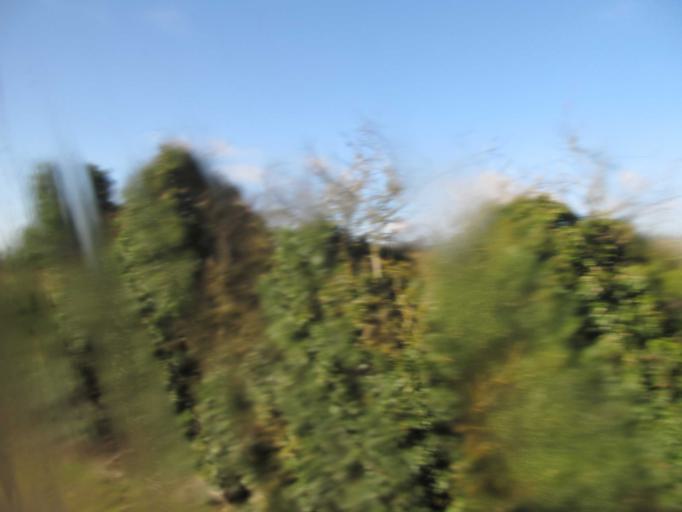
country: GB
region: England
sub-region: Hampshire
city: Kings Worthy
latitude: 51.1449
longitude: -1.3422
